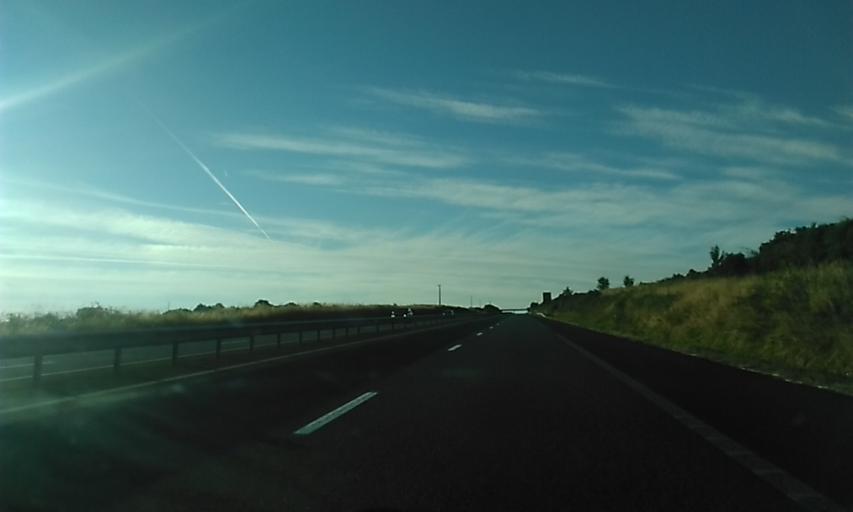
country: FR
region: Brittany
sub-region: Departement d'Ille-et-Vilaine
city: Plelan-le-Grand
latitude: 47.9628
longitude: -2.0926
